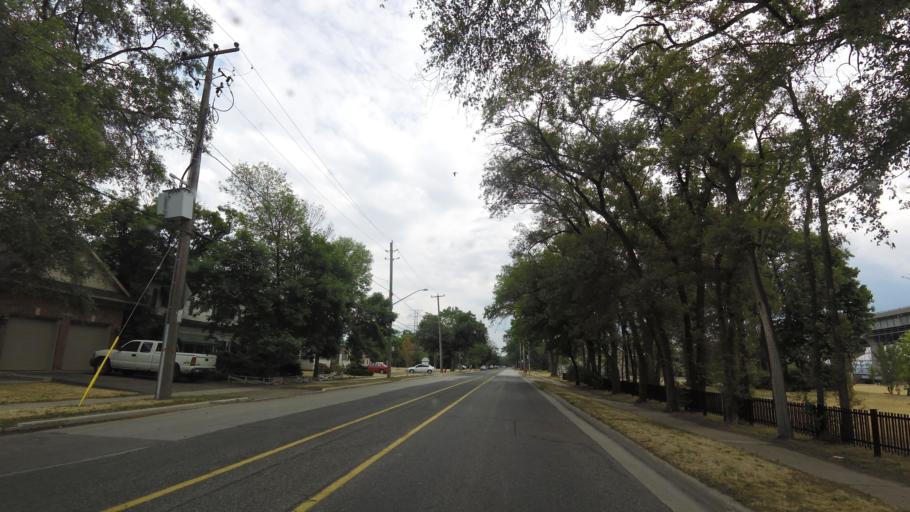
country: CA
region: Ontario
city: Hamilton
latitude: 43.2925
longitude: -79.7921
